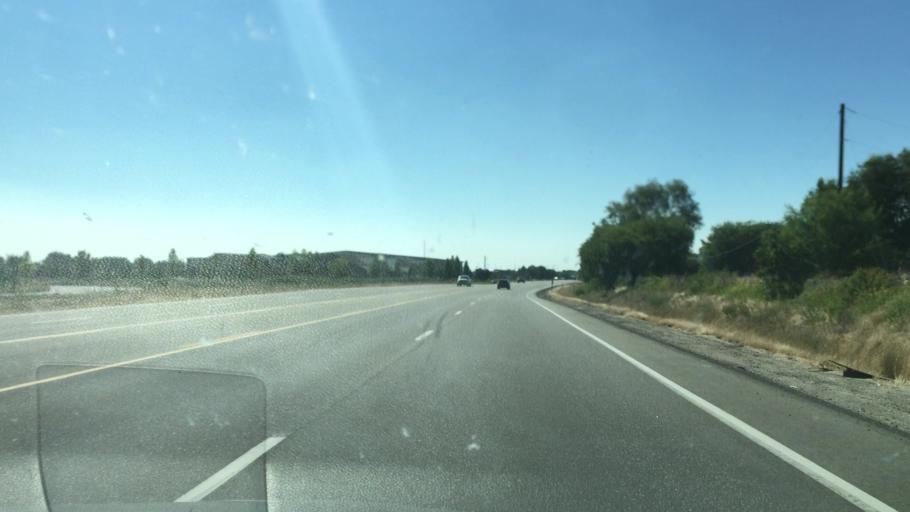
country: US
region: Idaho
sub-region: Ada County
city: Eagle
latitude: 43.6862
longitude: -116.3260
